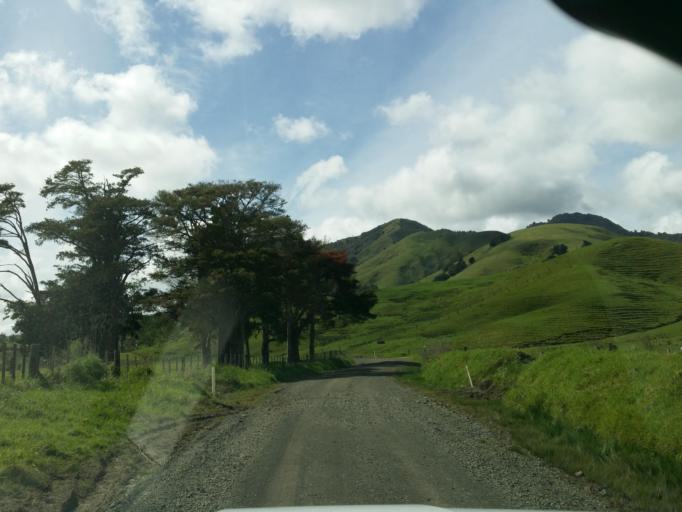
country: NZ
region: Northland
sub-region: Whangarei
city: Maungatapere
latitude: -35.8320
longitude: 174.0564
